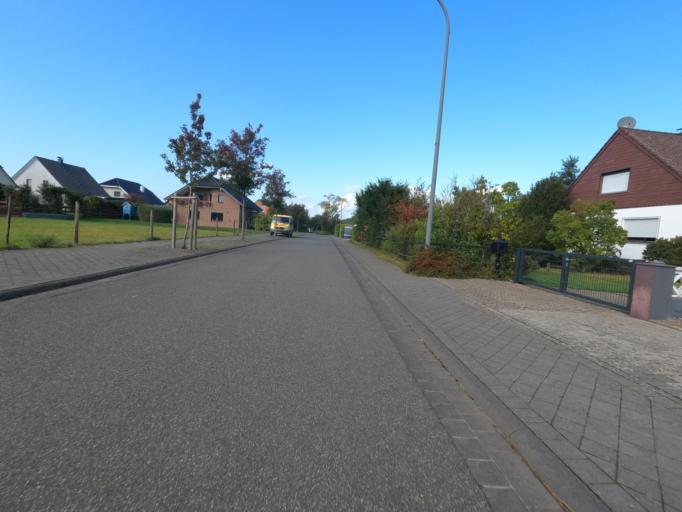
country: DE
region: North Rhine-Westphalia
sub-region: Regierungsbezirk Koln
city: Inden
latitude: 50.8801
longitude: 6.3973
